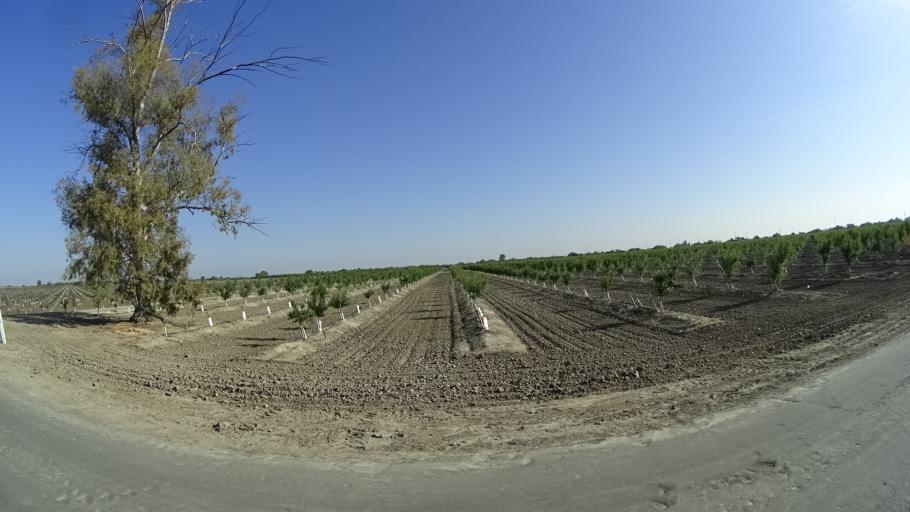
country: US
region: California
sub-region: Fresno County
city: Riverdale
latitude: 36.3802
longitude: -119.9095
